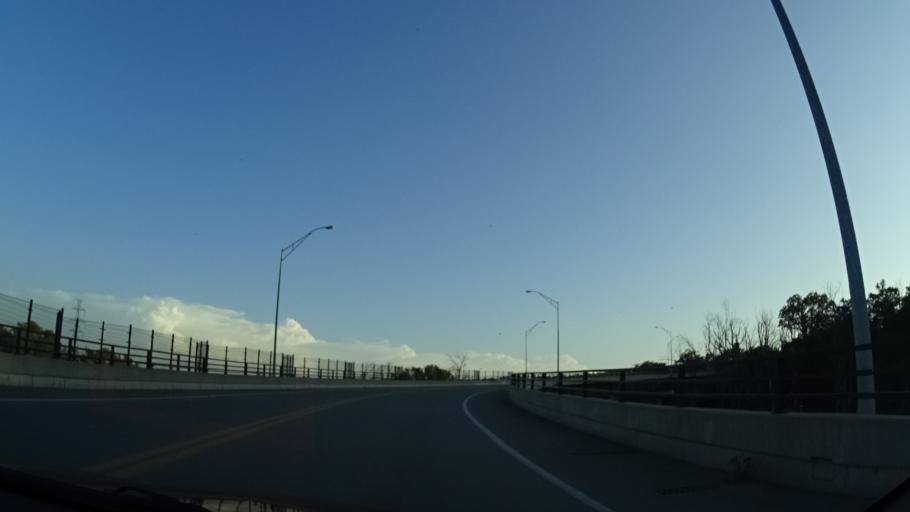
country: US
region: Nebraska
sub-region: Douglas County
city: Omaha
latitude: 41.2110
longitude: -95.9314
